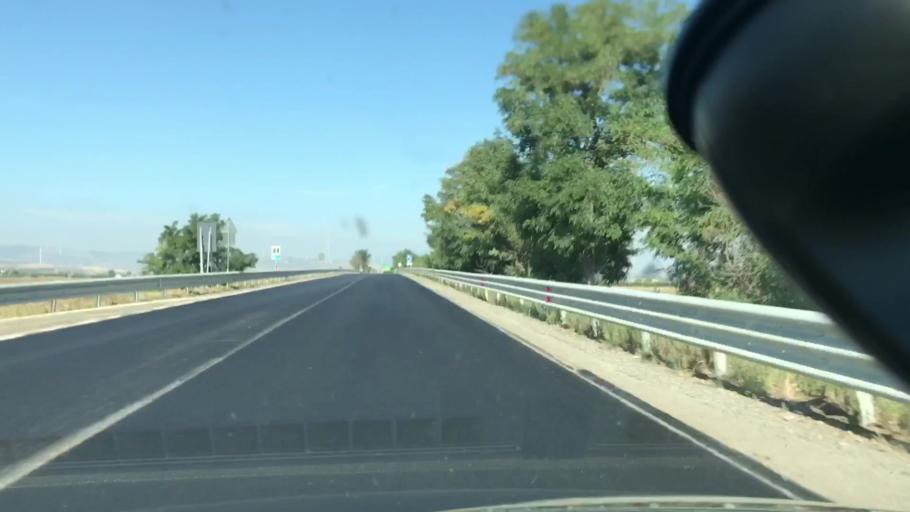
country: IT
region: Basilicate
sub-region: Provincia di Potenza
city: Zona 179
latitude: 41.0751
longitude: 15.6434
